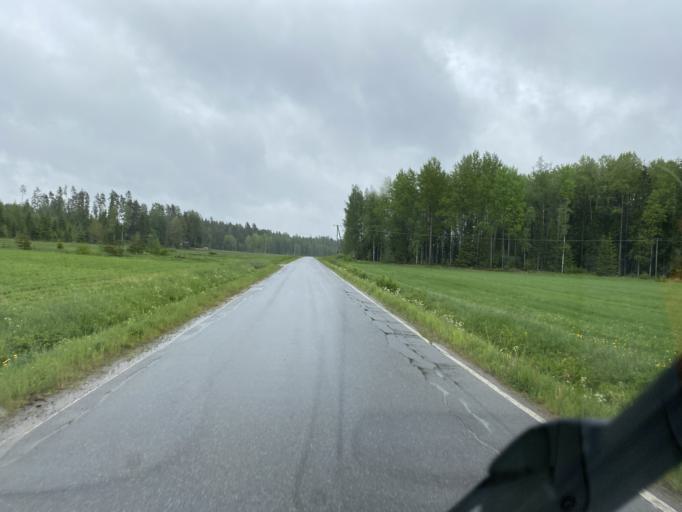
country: FI
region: Haeme
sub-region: Forssa
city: Humppila
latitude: 61.0503
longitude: 23.3541
